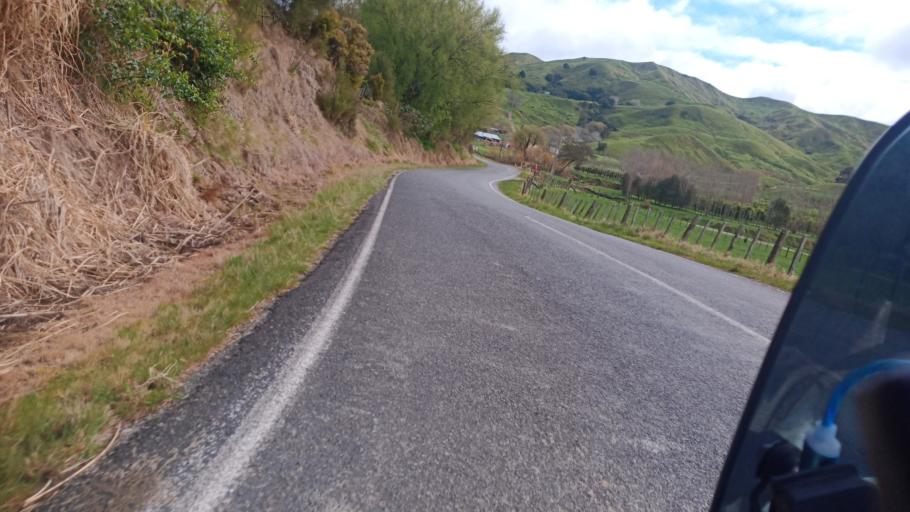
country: NZ
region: Gisborne
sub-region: Gisborne District
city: Gisborne
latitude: -38.5680
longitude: 178.1672
